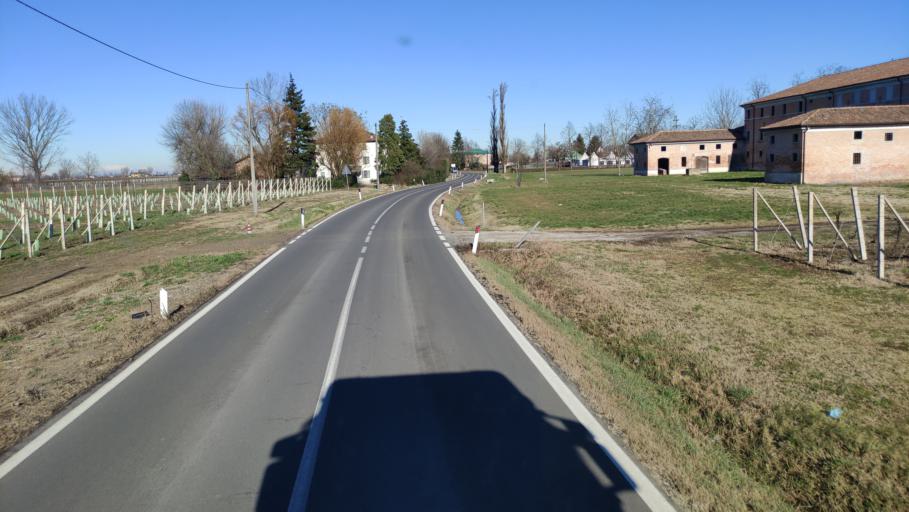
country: IT
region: Emilia-Romagna
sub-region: Provincia di Reggio Emilia
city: Rio Saliceto
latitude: 44.7982
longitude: 10.7782
